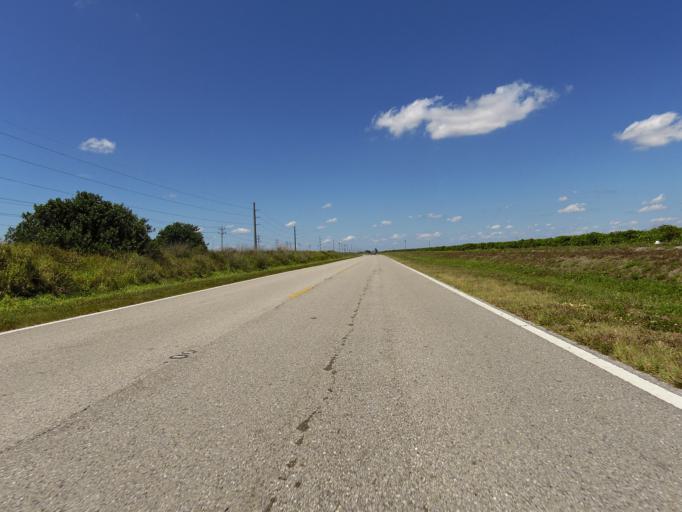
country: US
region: Florida
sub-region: Collier County
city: Immokalee
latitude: 26.3124
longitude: -81.4162
